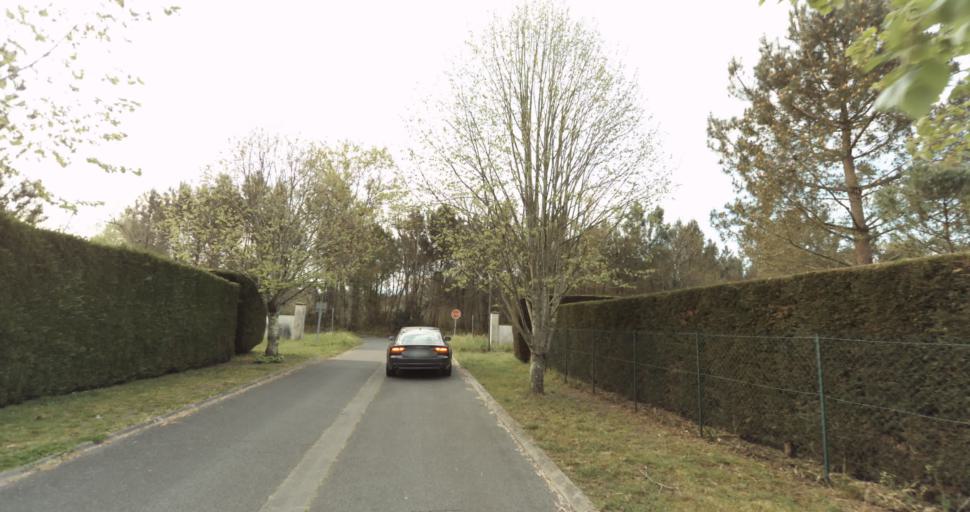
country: FR
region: Aquitaine
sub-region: Departement de la Gironde
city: Saint-Aubin-de-Medoc
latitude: 44.7746
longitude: -0.7366
